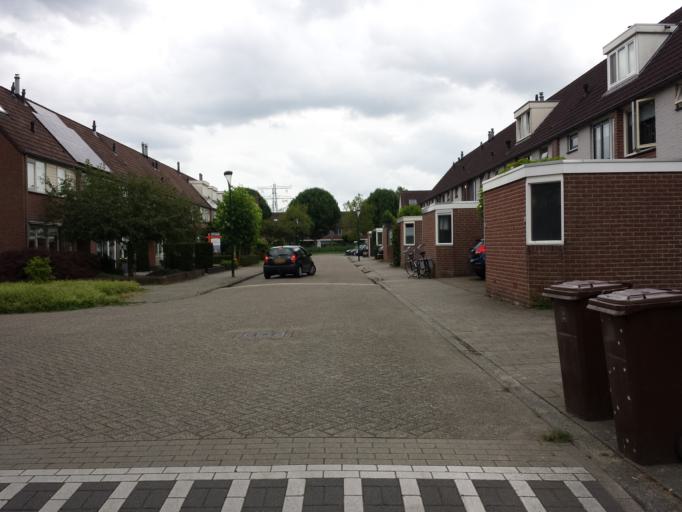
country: NL
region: Utrecht
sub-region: Gemeente Veenendaal
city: Veenendaal
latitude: 52.0310
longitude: 5.5266
